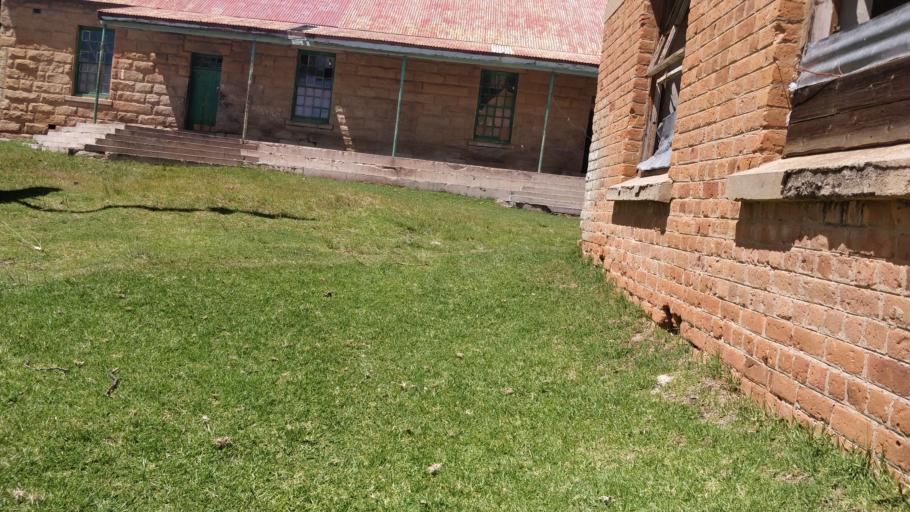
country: LS
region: Maseru
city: Nako
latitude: -29.6318
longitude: 27.5052
